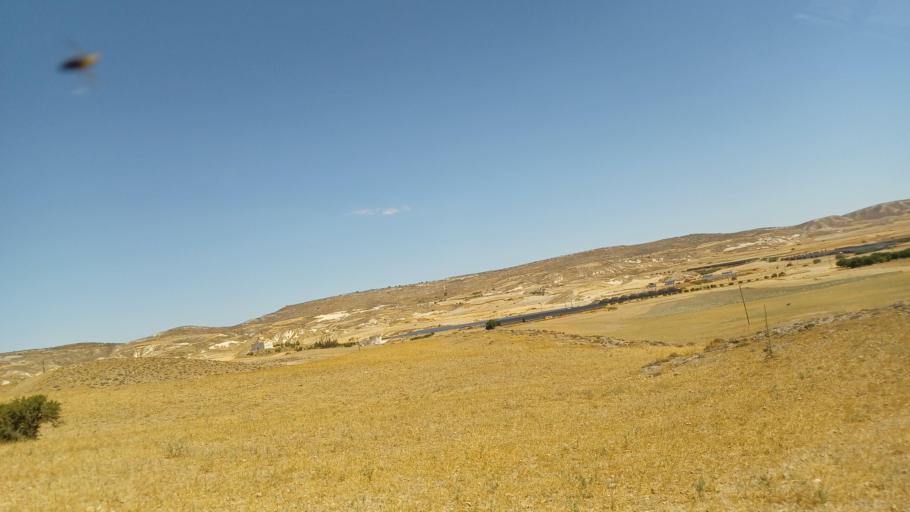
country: CY
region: Larnaka
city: Troulloi
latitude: 35.0220
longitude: 33.5991
